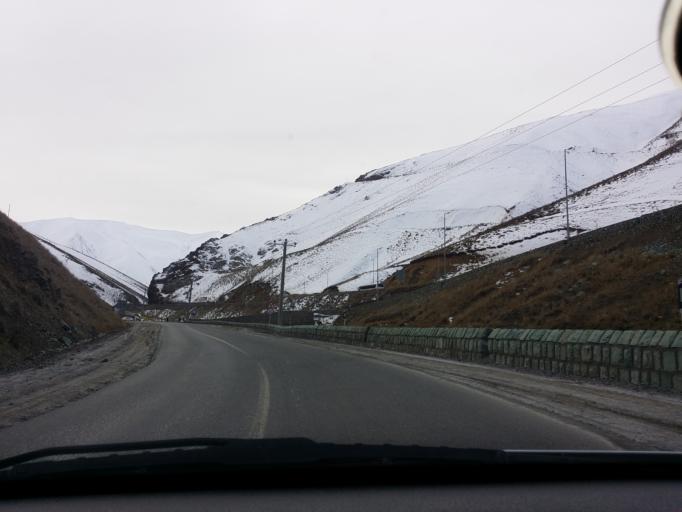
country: IR
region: Tehran
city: Tajrish
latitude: 36.1740
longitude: 51.3151
